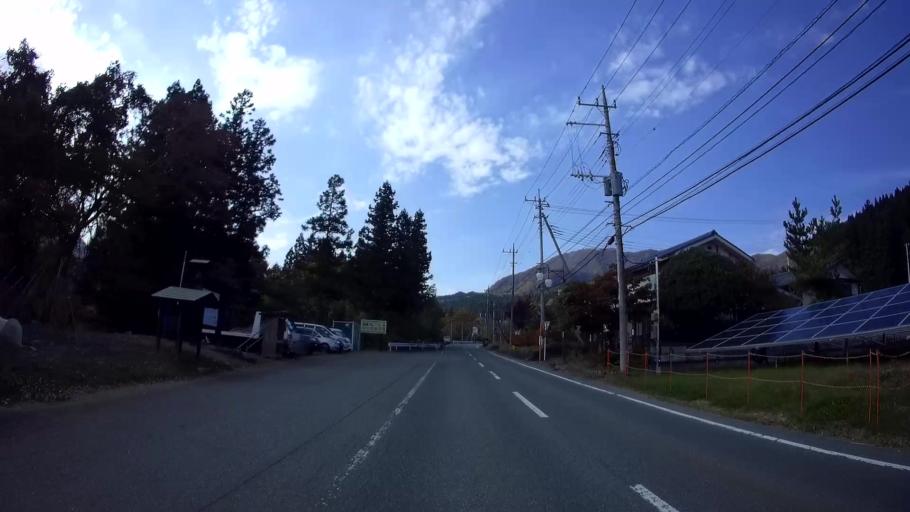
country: JP
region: Gunma
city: Nakanojomachi
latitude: 36.5068
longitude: 138.7070
